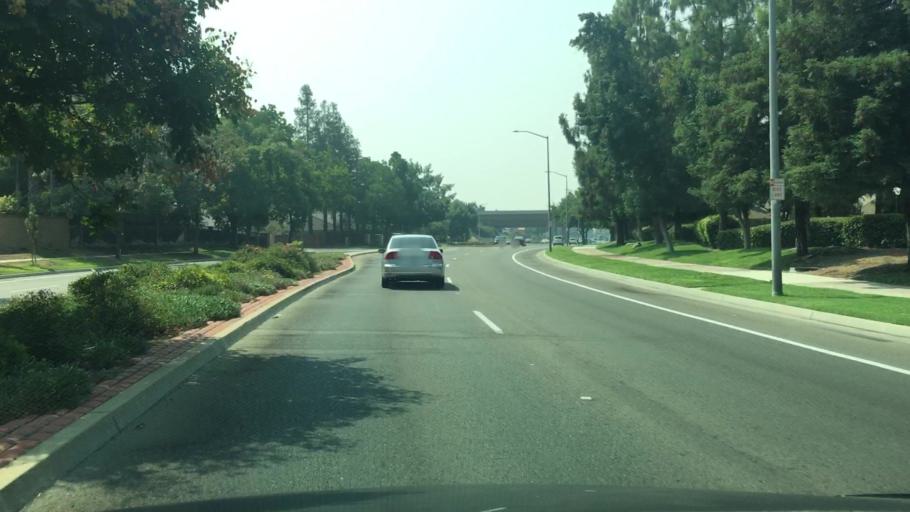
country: US
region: California
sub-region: Fresno County
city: Clovis
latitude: 36.8425
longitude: -119.7001
